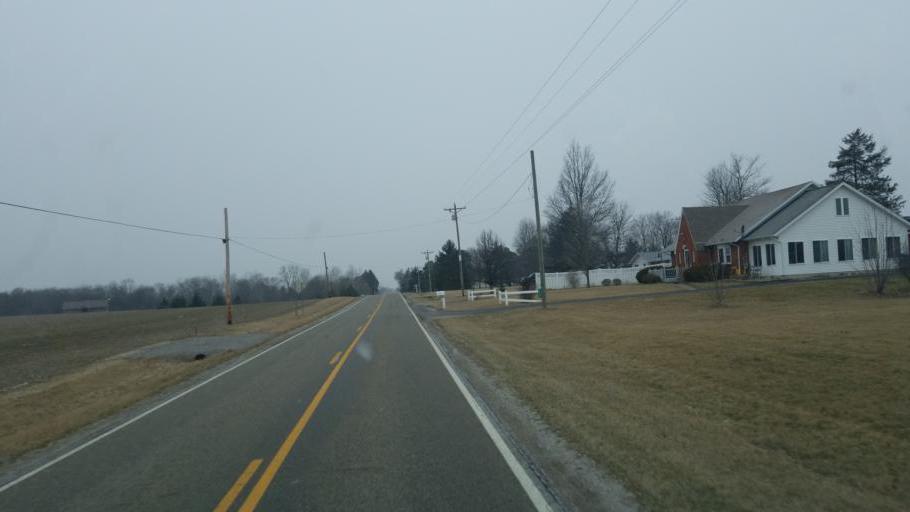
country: US
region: Ohio
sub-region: Defiance County
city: Hicksville
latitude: 41.3248
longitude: -84.7500
